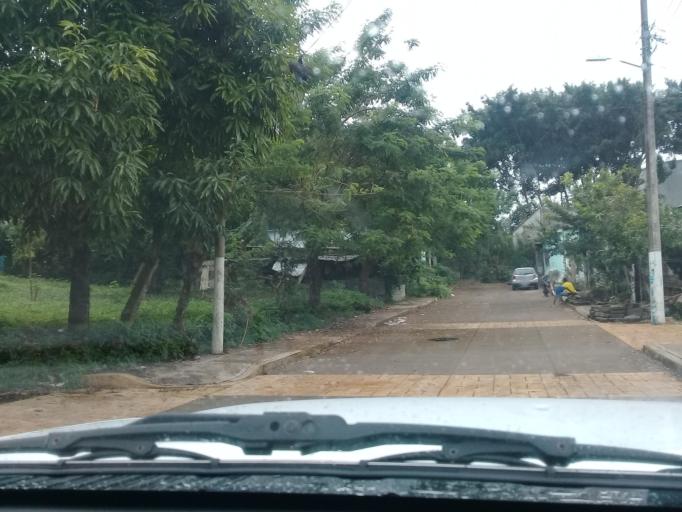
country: MX
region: Veracruz
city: San Andres Tuxtla
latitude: 18.4395
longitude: -95.2071
